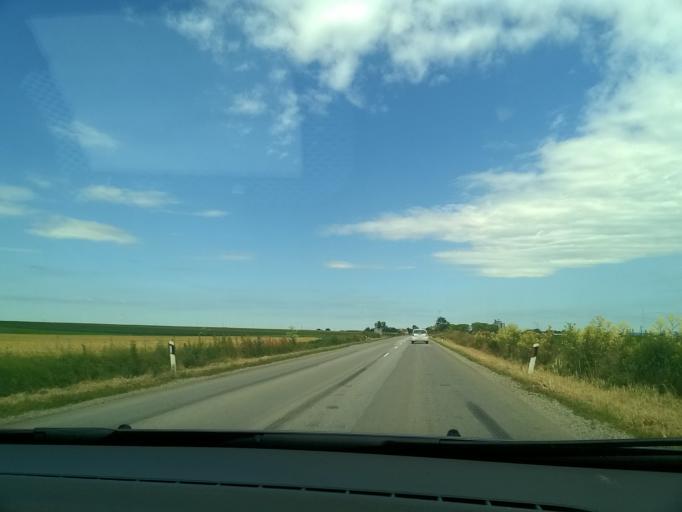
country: RS
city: Putinci
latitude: 44.9976
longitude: 19.9518
